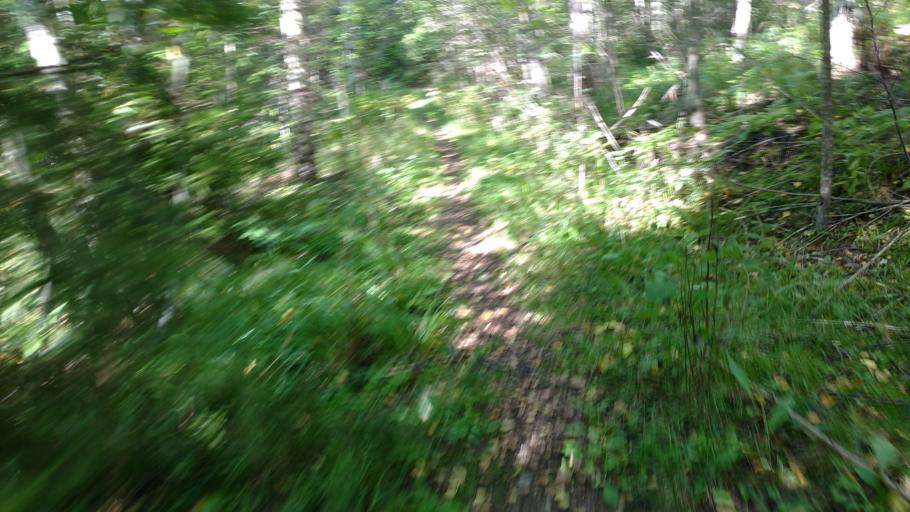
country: FI
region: Varsinais-Suomi
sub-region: Salo
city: Salo
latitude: 60.3538
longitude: 23.1302
